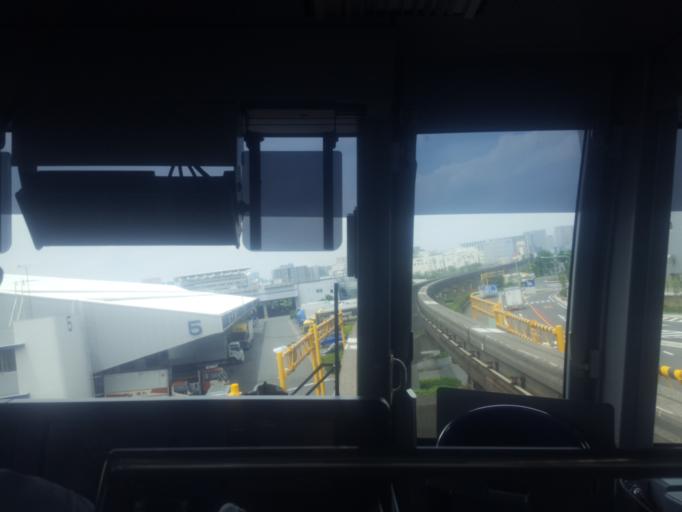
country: JP
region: Kanagawa
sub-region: Kawasaki-shi
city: Kawasaki
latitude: 35.5871
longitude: 139.7468
